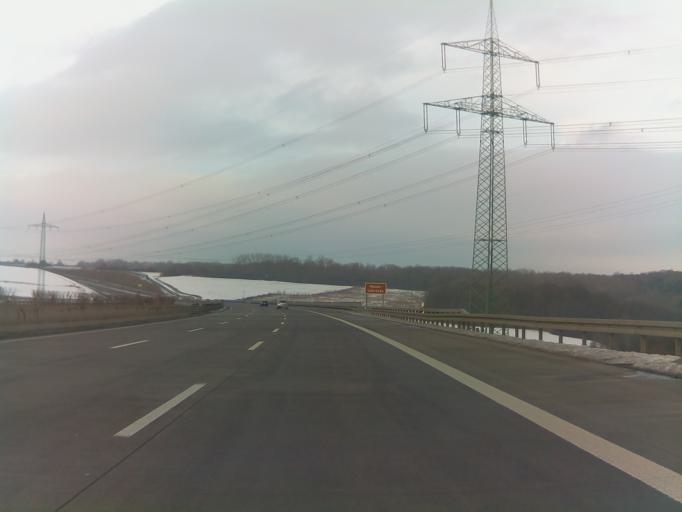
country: DE
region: Thuringia
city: Haina
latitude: 50.9751
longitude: 10.4867
